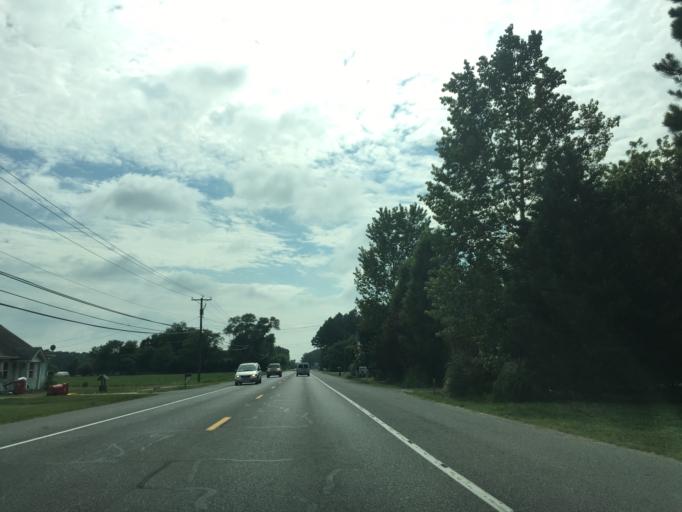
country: US
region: Delaware
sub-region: Sussex County
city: Millsboro
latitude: 38.5532
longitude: -75.2169
